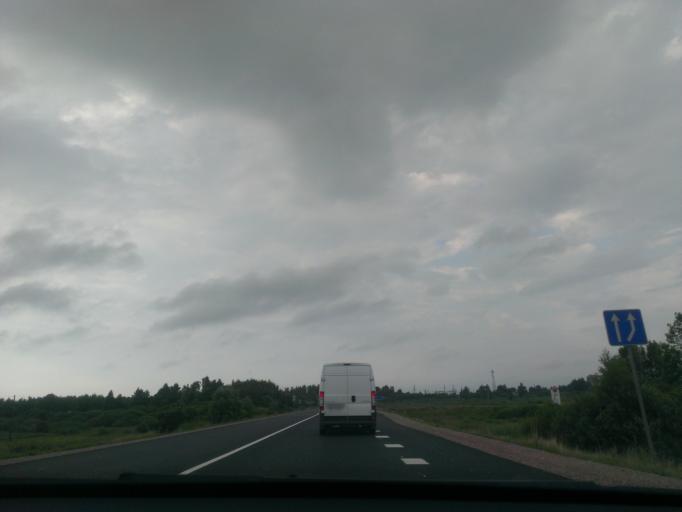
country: LV
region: Lecava
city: Iecava
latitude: 56.6225
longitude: 24.2194
